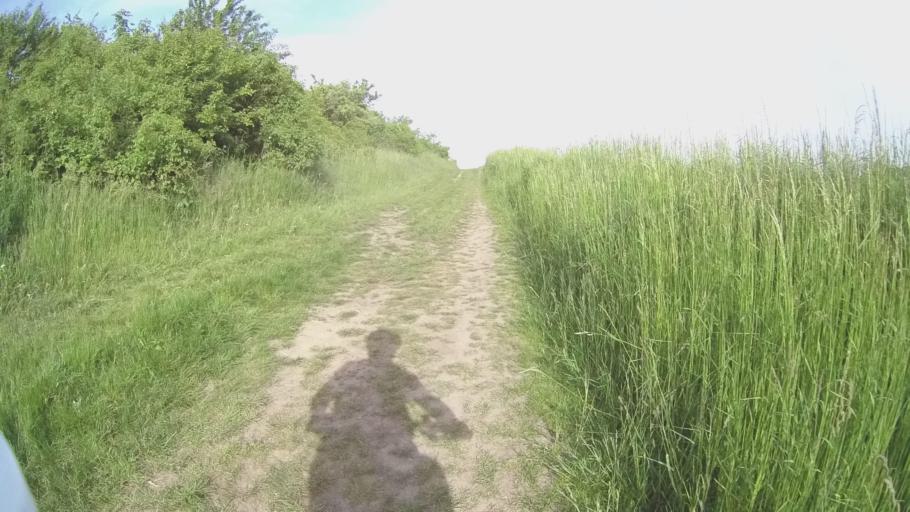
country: CZ
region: Praha
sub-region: Praha 19
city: Kbely
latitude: 50.1670
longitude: 14.5536
